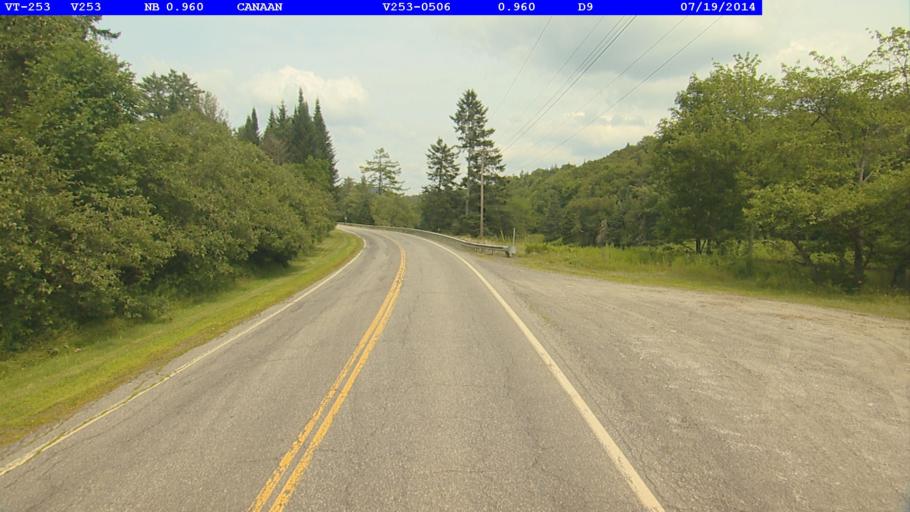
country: US
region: New Hampshire
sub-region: Coos County
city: Colebrook
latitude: 45.0025
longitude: -71.5217
